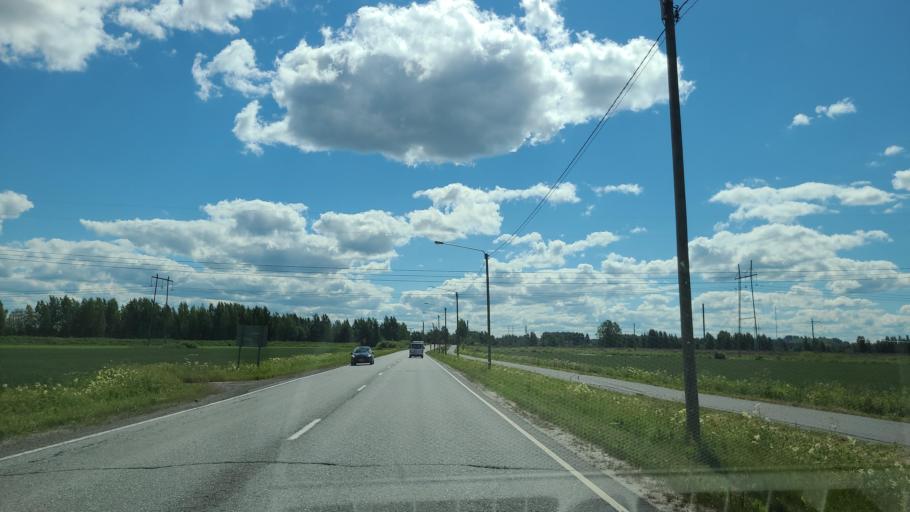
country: FI
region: Southern Ostrobothnia
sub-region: Seinaejoki
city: Seinaejoki
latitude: 62.8073
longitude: 22.8150
